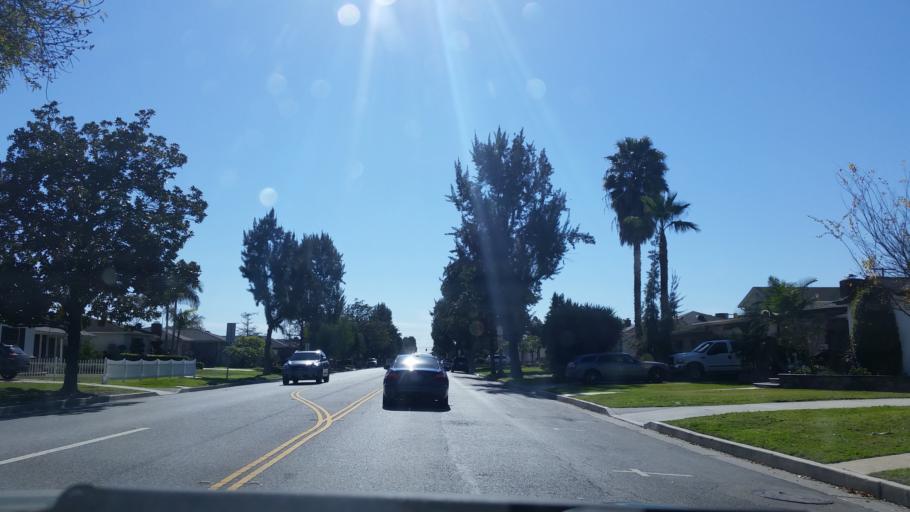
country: US
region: California
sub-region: Los Angeles County
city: Lakewood
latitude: 33.8394
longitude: -118.1339
